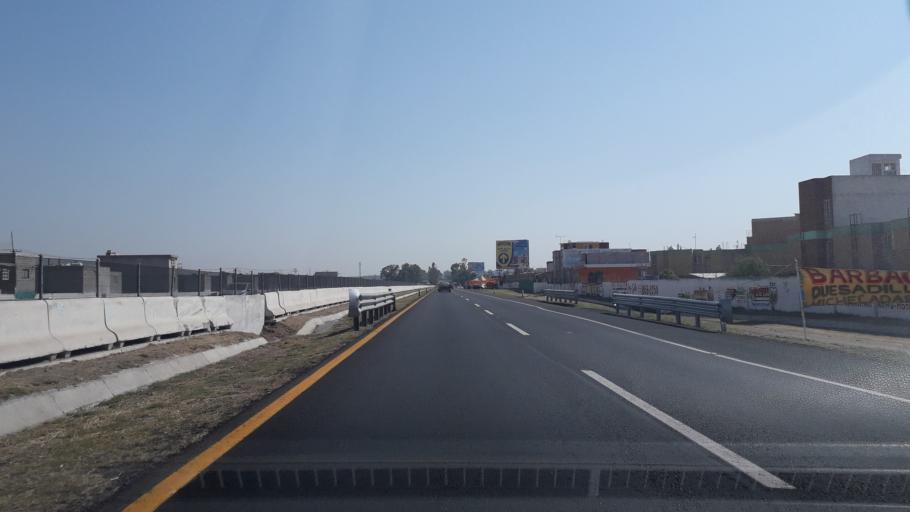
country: MX
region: Mexico
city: Santo Tomas Chiconautla
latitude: 19.6354
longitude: -99.0207
